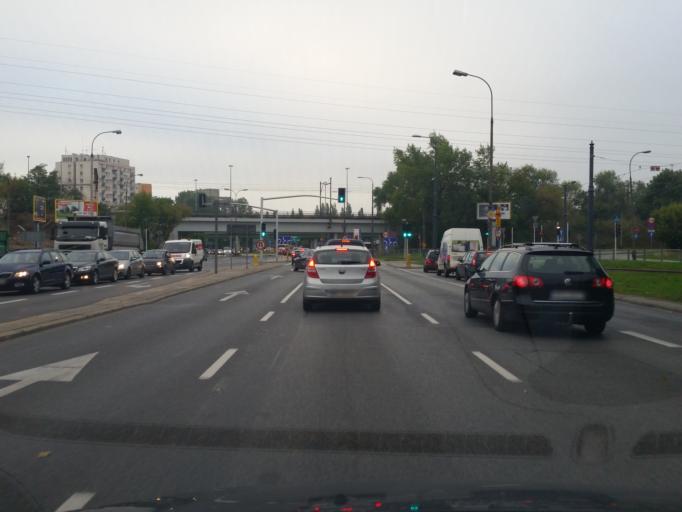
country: PL
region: Masovian Voivodeship
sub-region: Warszawa
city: Praga Polnoc
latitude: 52.2659
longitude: 21.0206
